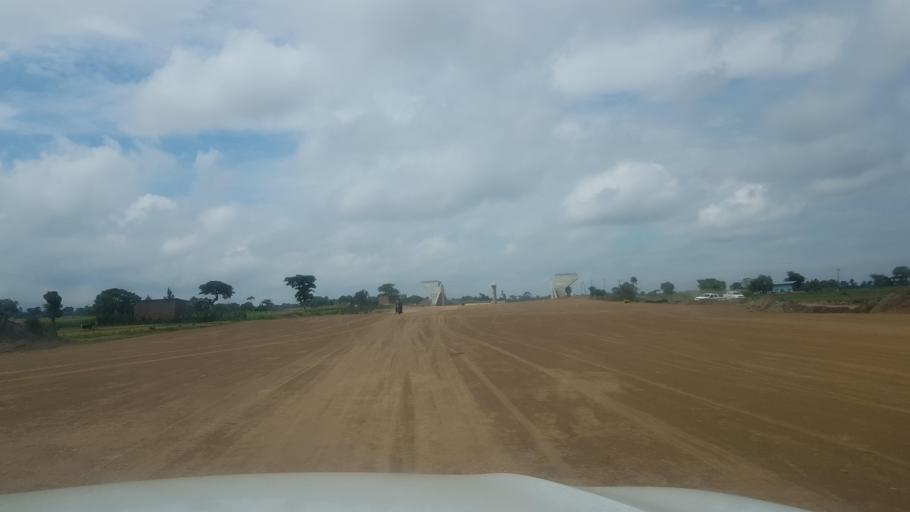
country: ET
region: Oromiya
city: Shashemene
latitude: 7.2582
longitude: 38.5949
